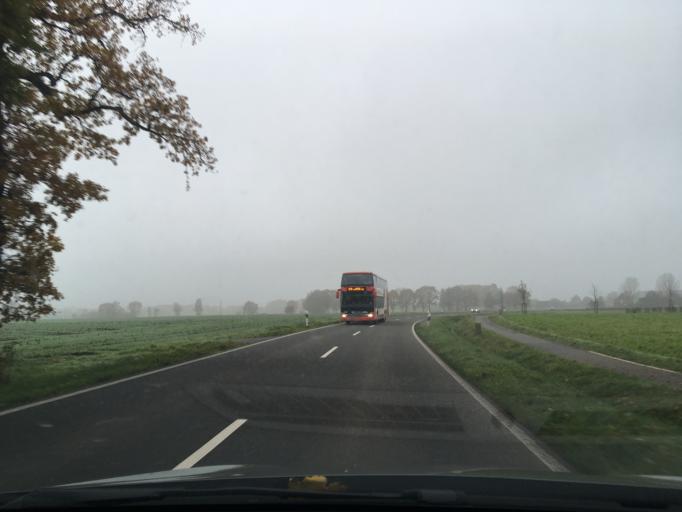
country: DE
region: North Rhine-Westphalia
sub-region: Regierungsbezirk Munster
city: Ahaus
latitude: 52.0780
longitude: 6.9347
